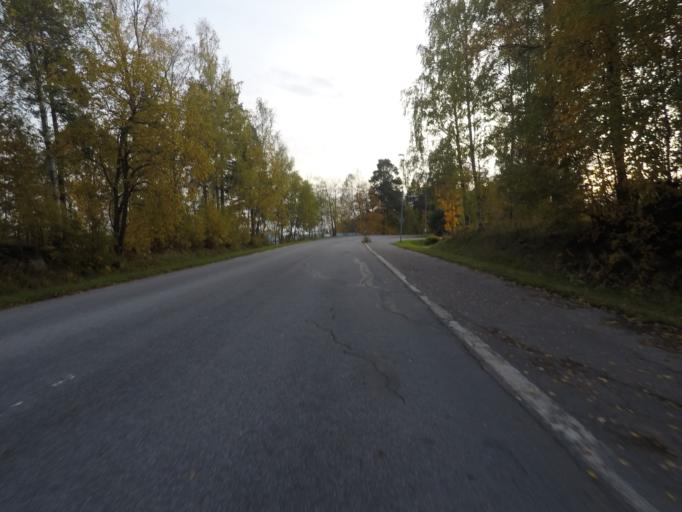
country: SE
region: OErebro
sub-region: Karlskoga Kommun
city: Karlskoga
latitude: 59.3018
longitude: 14.4919
